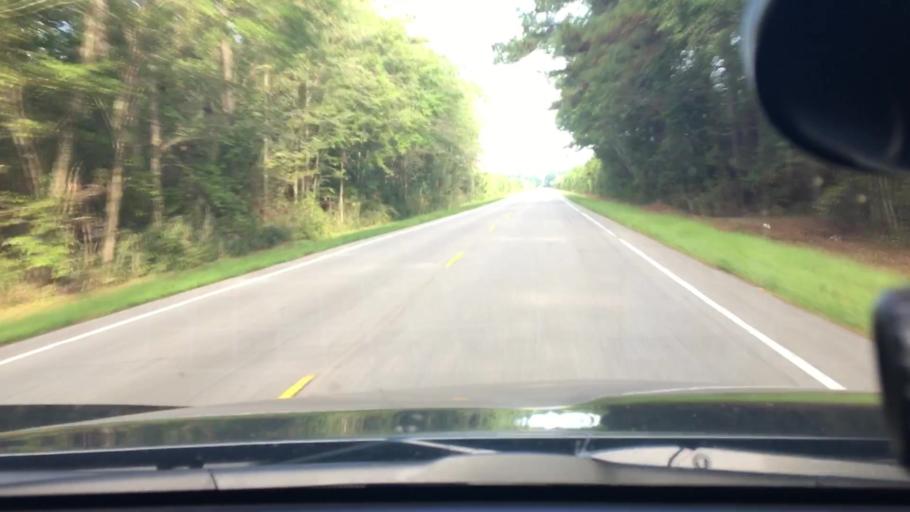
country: US
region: North Carolina
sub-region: Edgecombe County
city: Pinetops
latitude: 35.7684
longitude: -77.5677
